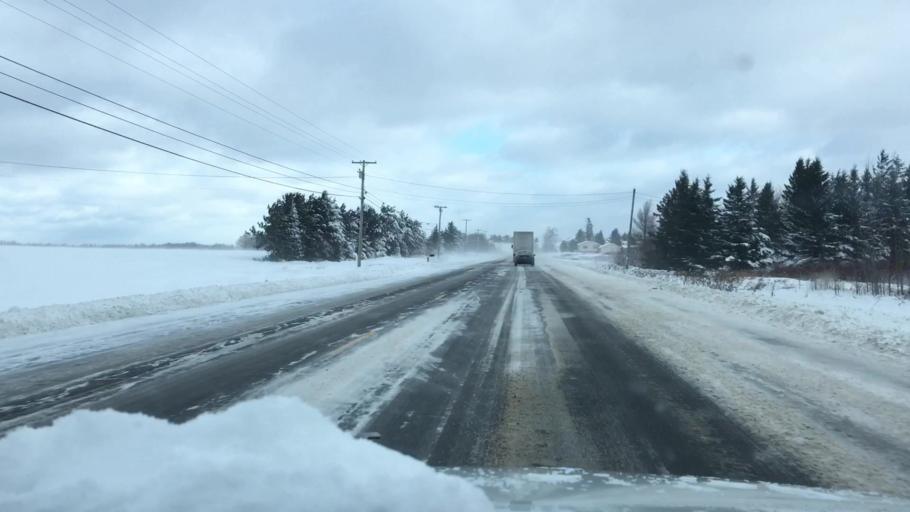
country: US
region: Maine
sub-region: Aroostook County
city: Presque Isle
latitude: 46.7380
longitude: -67.9984
